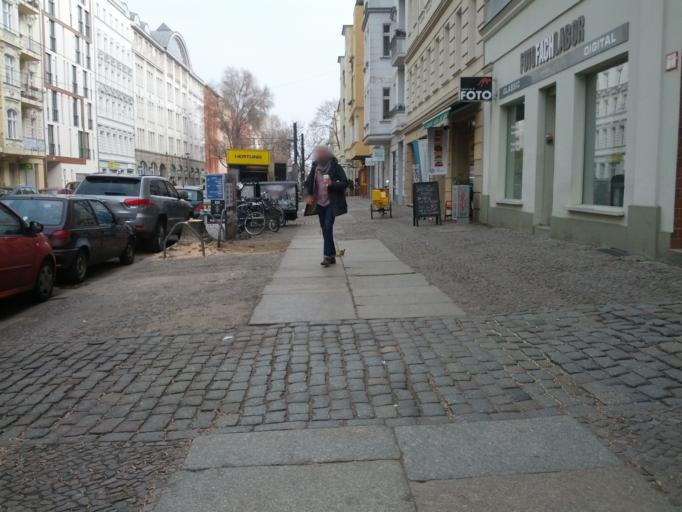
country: DE
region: Berlin
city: Prenzlauer Berg Bezirk
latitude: 52.5422
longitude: 13.4137
